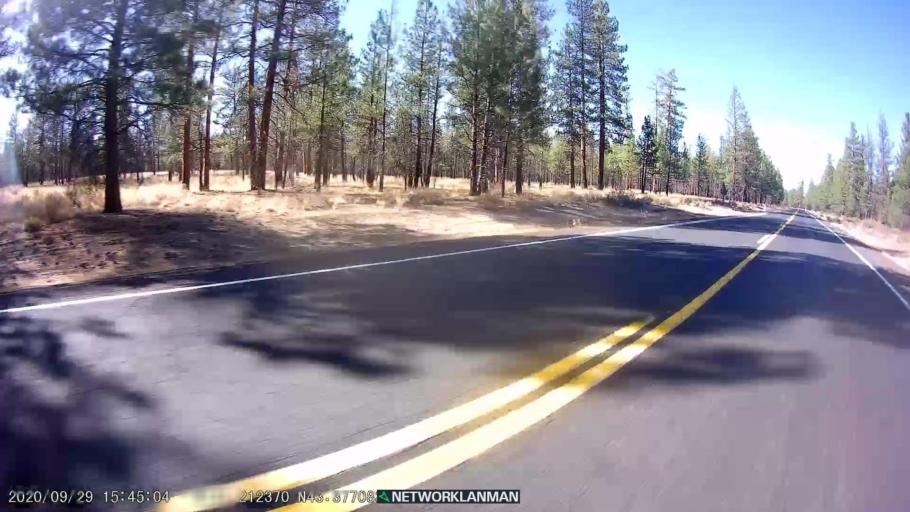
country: US
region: Oregon
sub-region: Deschutes County
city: La Pine
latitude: 43.3772
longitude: -121.2124
